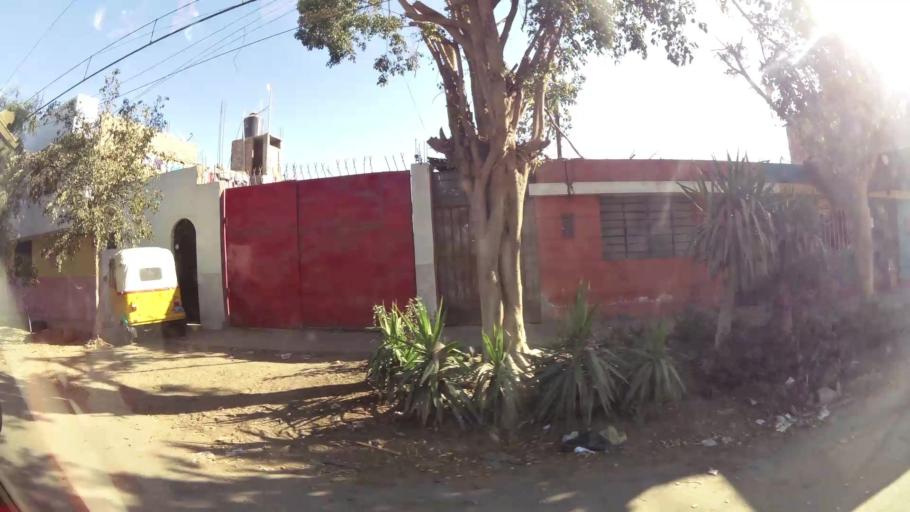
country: PE
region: Ica
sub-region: Provincia de Ica
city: La Tinguina
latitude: -14.0428
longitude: -75.7026
